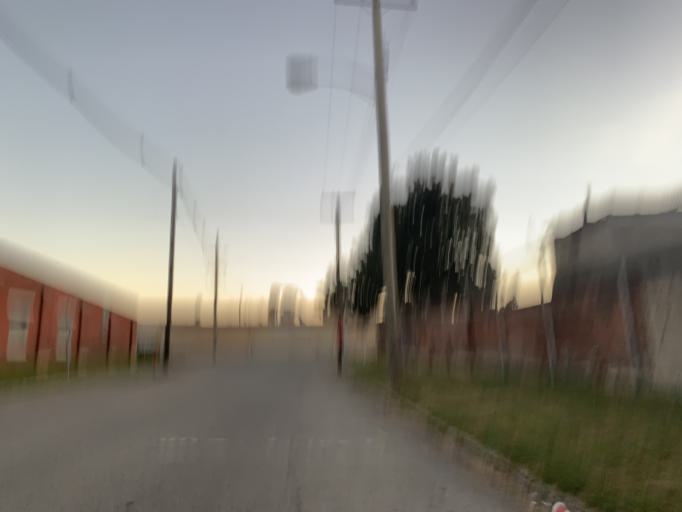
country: US
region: Kentucky
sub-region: Jefferson County
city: Louisville
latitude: 38.2308
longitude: -85.7726
